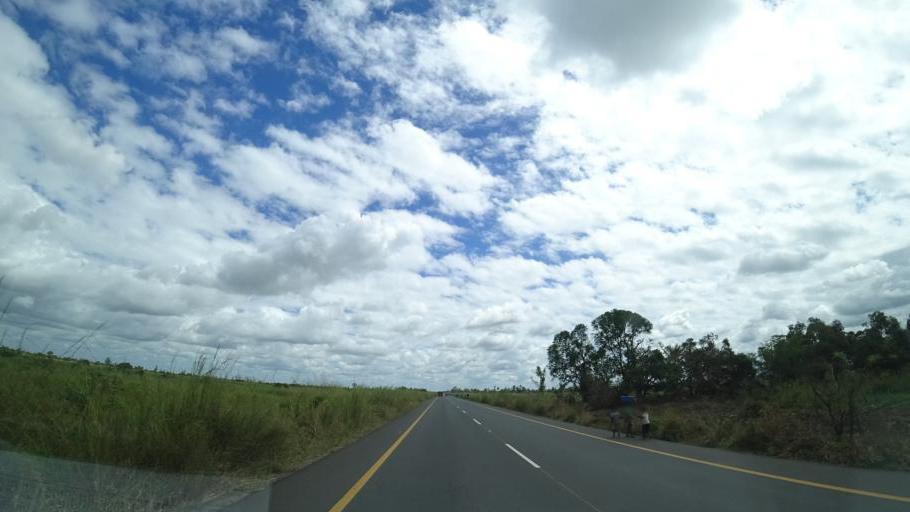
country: MZ
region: Sofala
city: Dondo
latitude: -19.3884
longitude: 34.4145
